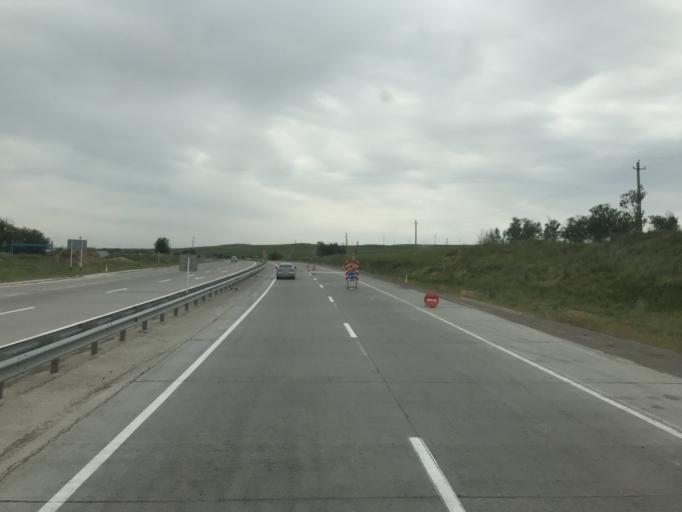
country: KZ
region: Ongtustik Qazaqstan
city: Qazyqurt
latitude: 41.8645
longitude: 69.4130
